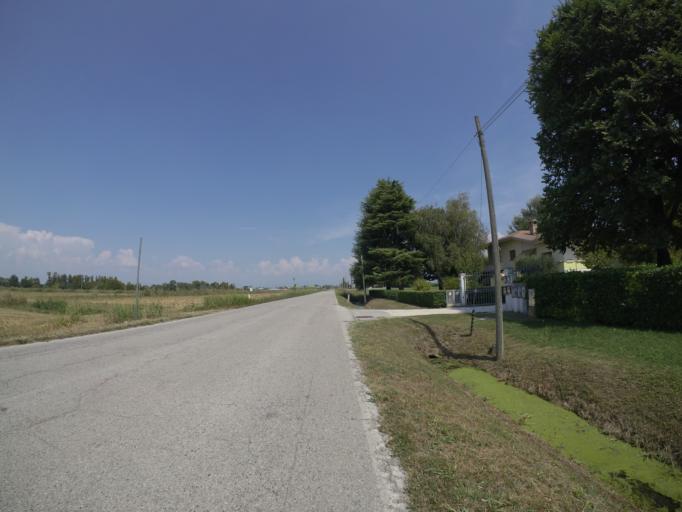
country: IT
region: Friuli Venezia Giulia
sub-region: Provincia di Udine
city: Pocenia
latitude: 45.8547
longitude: 13.1049
